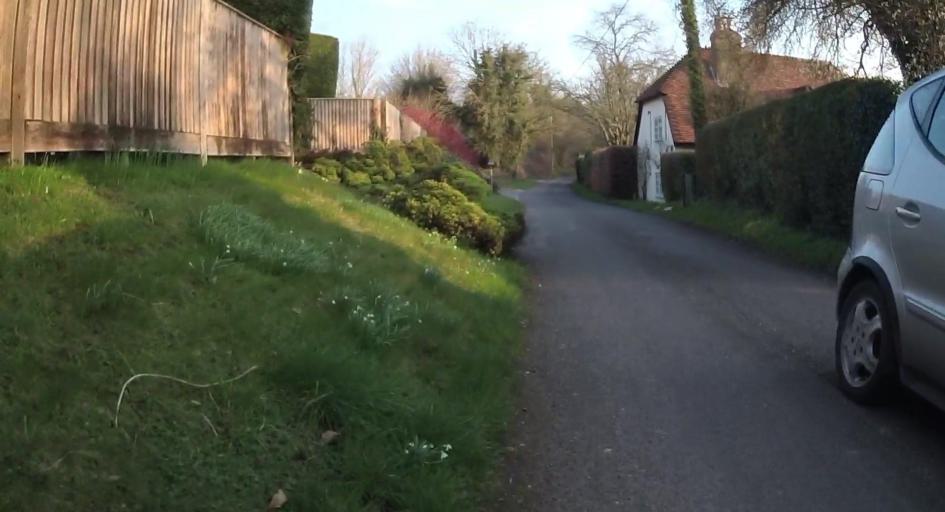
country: GB
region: England
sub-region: Hampshire
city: Alton
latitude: 51.1724
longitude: -1.0031
